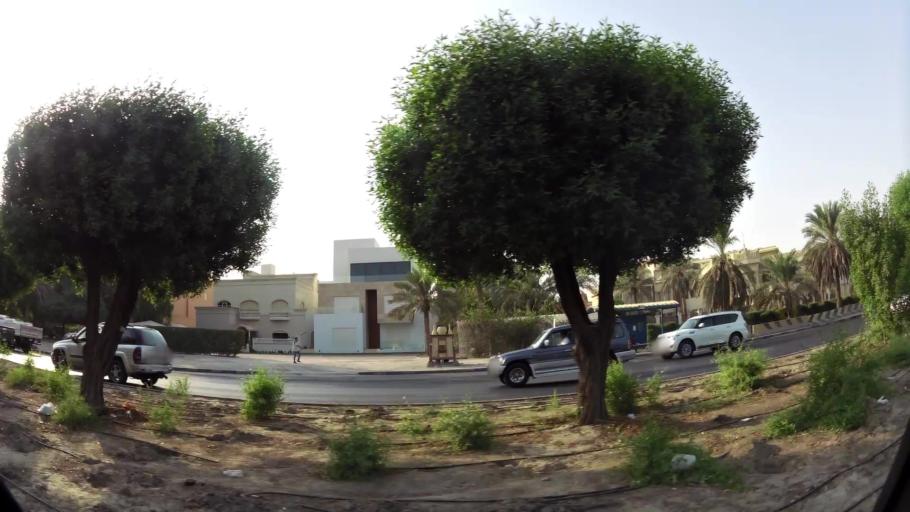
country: KW
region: Al Asimah
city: Ash Shamiyah
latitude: 29.3199
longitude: 47.9863
